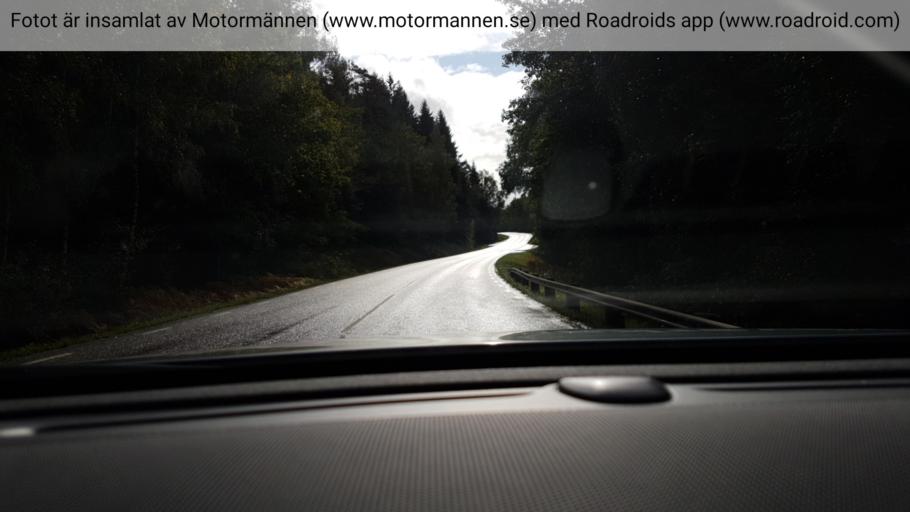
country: SE
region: Vaestra Goetaland
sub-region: Marks Kommun
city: Kinna
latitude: 57.4030
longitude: 12.7797
